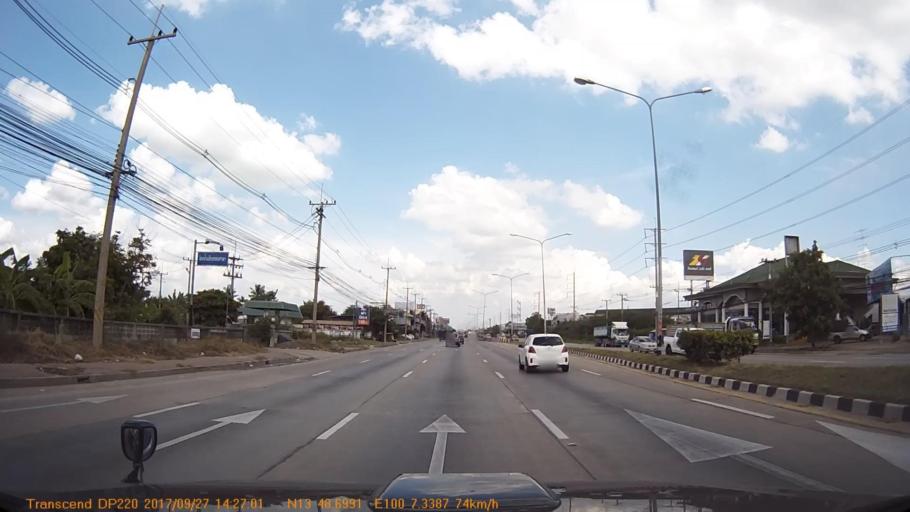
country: TH
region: Nakhon Pathom
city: Nakhon Chai Si
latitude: 13.8117
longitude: 100.1224
